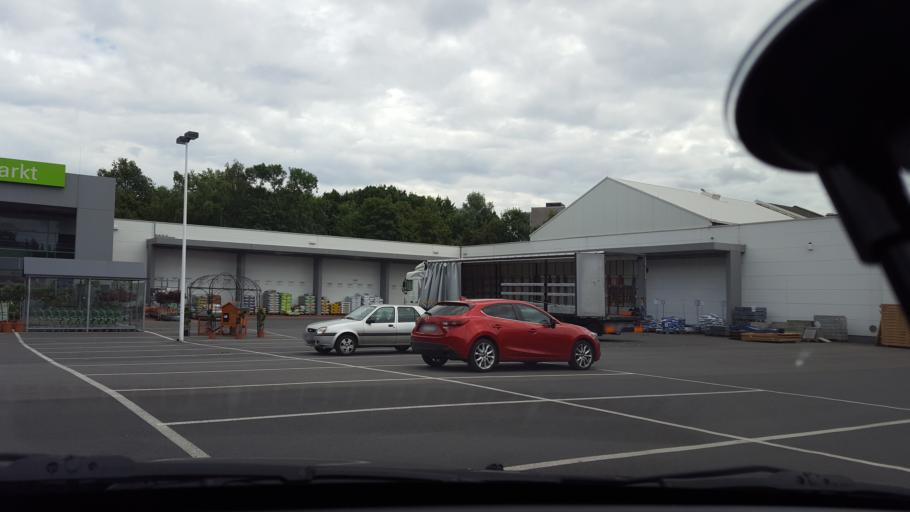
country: DE
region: North Rhine-Westphalia
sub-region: Regierungsbezirk Munster
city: Recklinghausen
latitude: 51.6245
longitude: 7.2108
